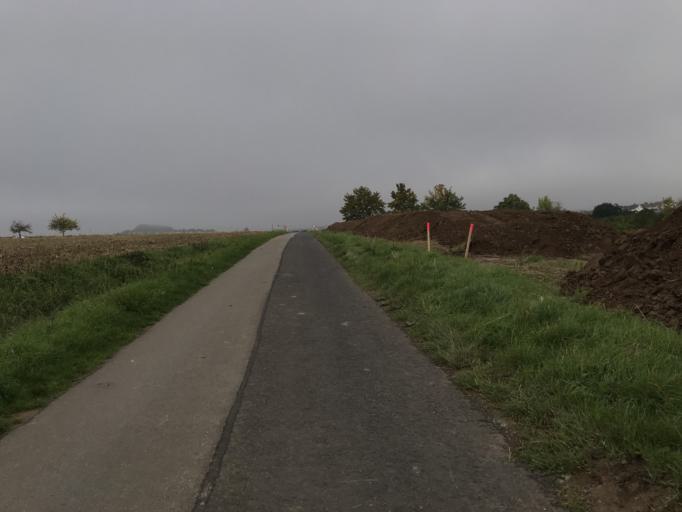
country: DE
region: Hesse
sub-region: Regierungsbezirk Kassel
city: Guxhagen
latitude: 51.2072
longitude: 9.4400
